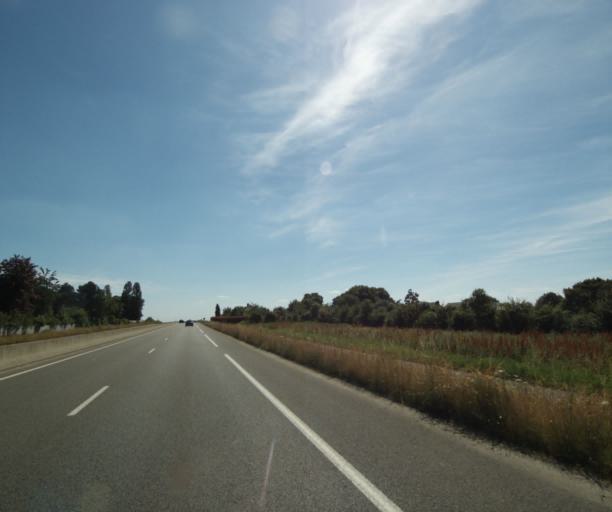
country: FR
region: Pays de la Loire
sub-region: Departement de la Mayenne
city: Laval
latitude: 48.0496
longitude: -0.7963
